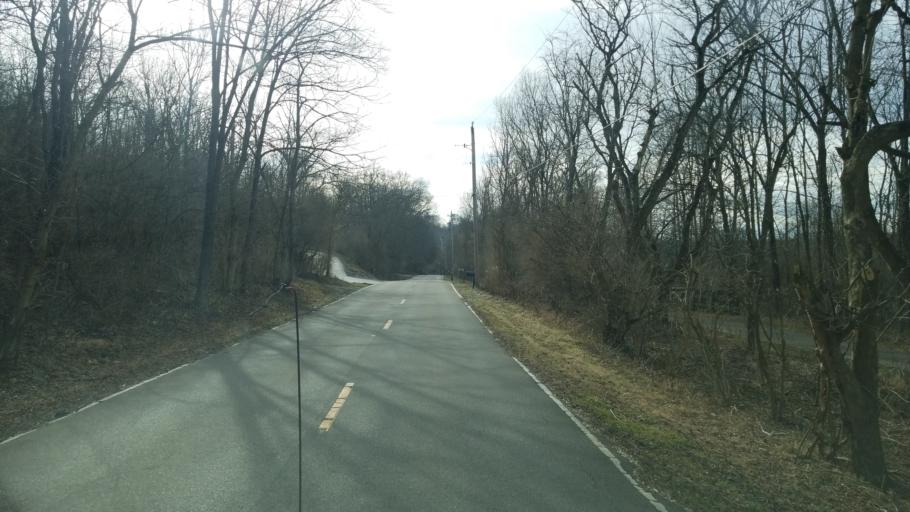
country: US
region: Ohio
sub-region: Warren County
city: Morrow
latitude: 39.4385
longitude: -84.1010
